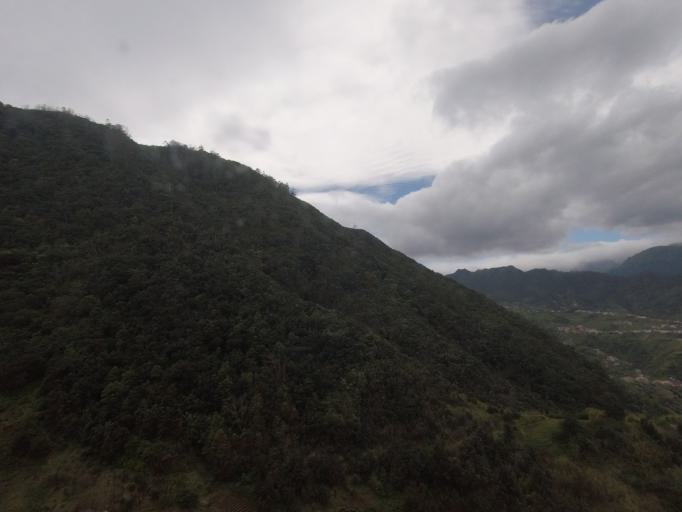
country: PT
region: Madeira
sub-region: Machico
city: Canical
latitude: 32.7621
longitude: -16.8080
